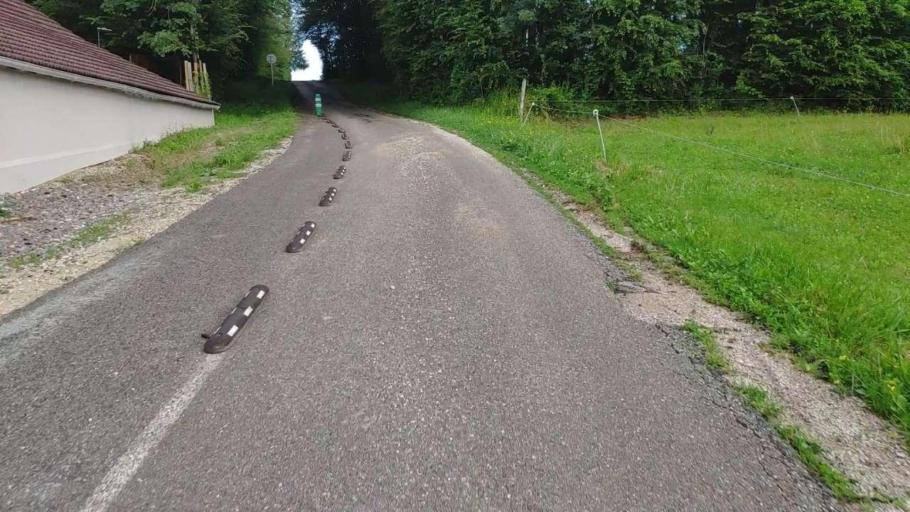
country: FR
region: Franche-Comte
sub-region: Departement du Jura
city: Poligny
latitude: 46.7997
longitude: 5.5971
